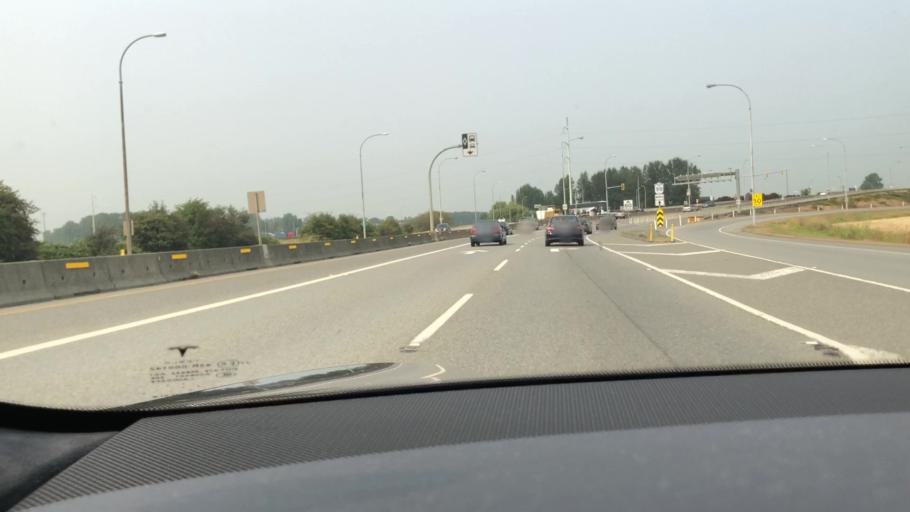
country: CA
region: British Columbia
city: Ladner
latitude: 49.1049
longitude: -123.0573
